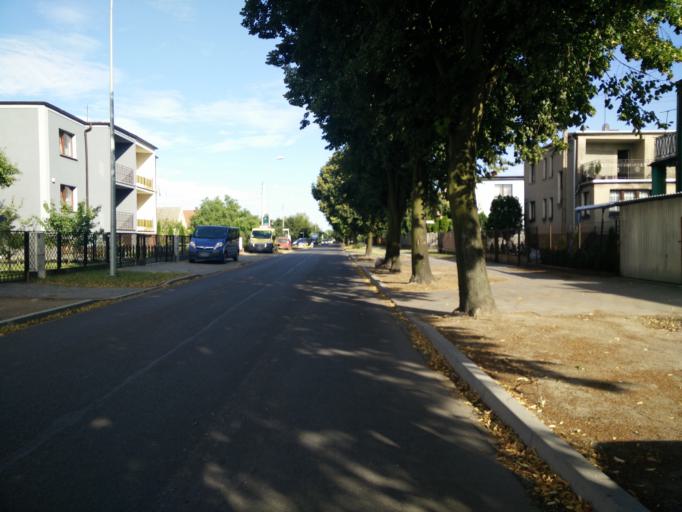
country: PL
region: Greater Poland Voivodeship
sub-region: Powiat sredzki
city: Sroda Wielkopolska
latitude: 52.2354
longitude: 17.2568
